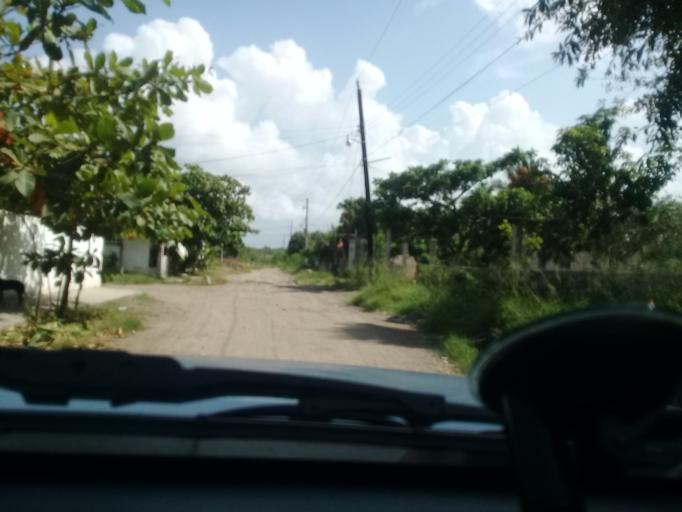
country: MX
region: Veracruz
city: Moralillo
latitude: 22.2287
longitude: -97.9033
